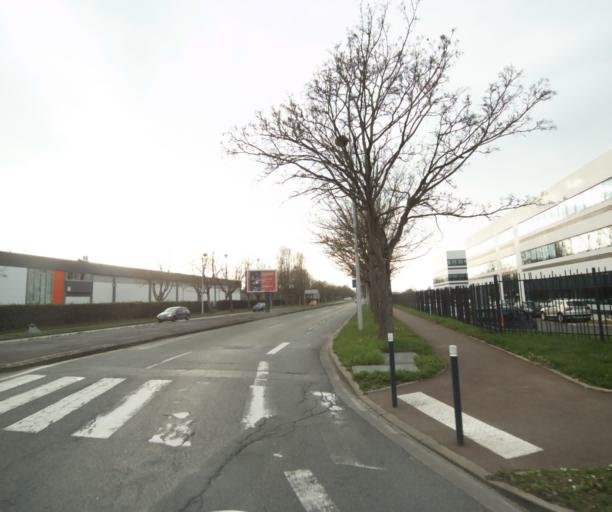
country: FR
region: Ile-de-France
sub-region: Departement du Val-d'Oise
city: Osny
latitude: 49.0522
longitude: 2.0459
